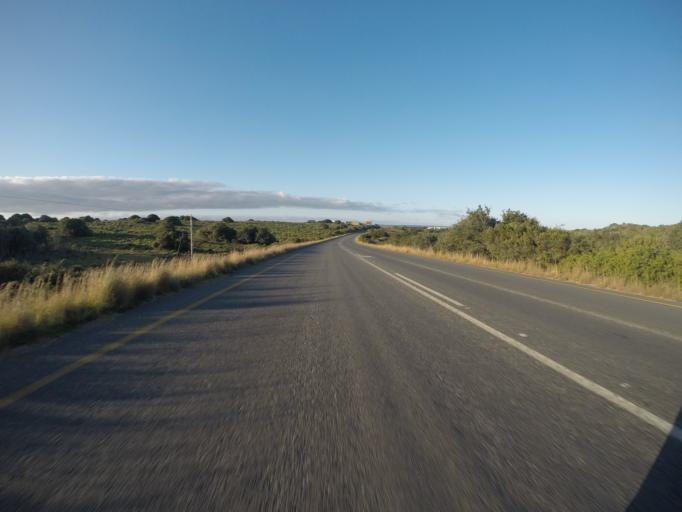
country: ZA
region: Western Cape
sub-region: Eden District Municipality
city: Riversdale
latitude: -34.3897
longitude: 21.3979
